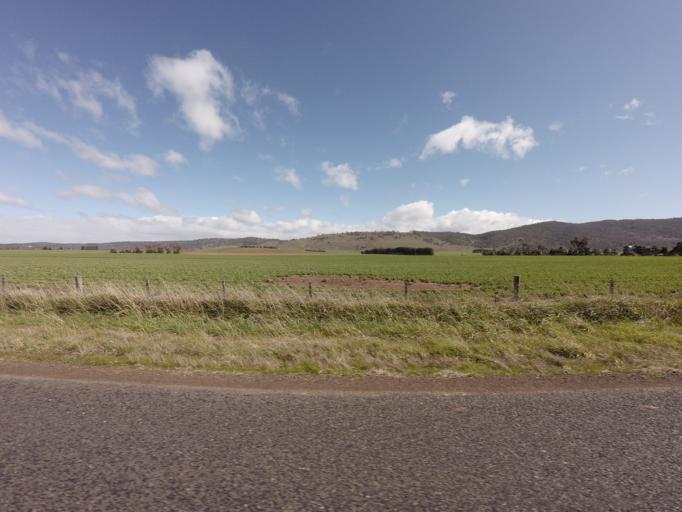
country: AU
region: Tasmania
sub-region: Northern Midlands
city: Evandale
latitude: -41.9999
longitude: 147.4557
